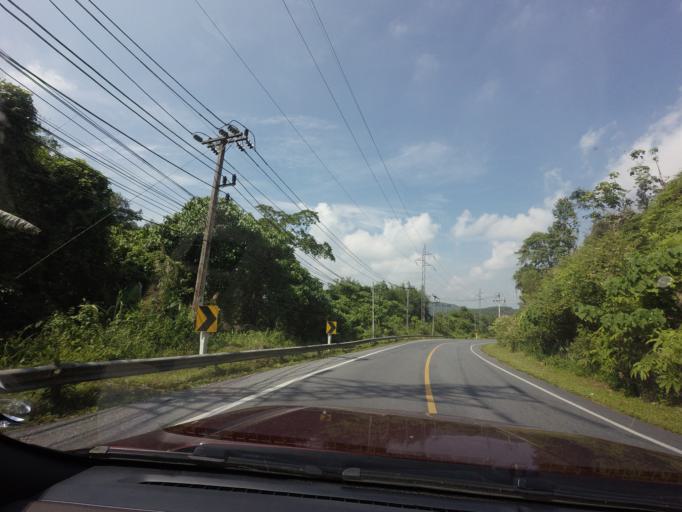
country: TH
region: Yala
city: Betong
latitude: 5.8357
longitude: 101.1196
